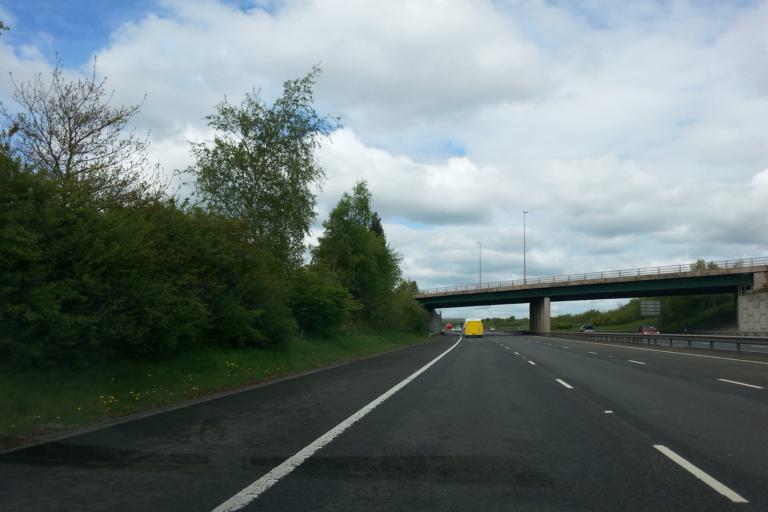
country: GB
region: England
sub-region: Staffordshire
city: Chasetown
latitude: 52.6554
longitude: -1.9022
